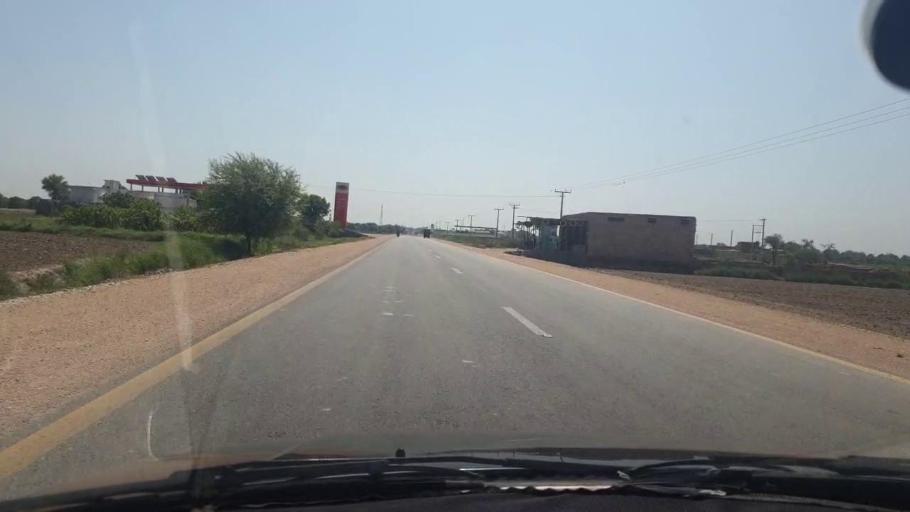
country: PK
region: Sindh
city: Chambar
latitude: 25.3133
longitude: 68.8054
